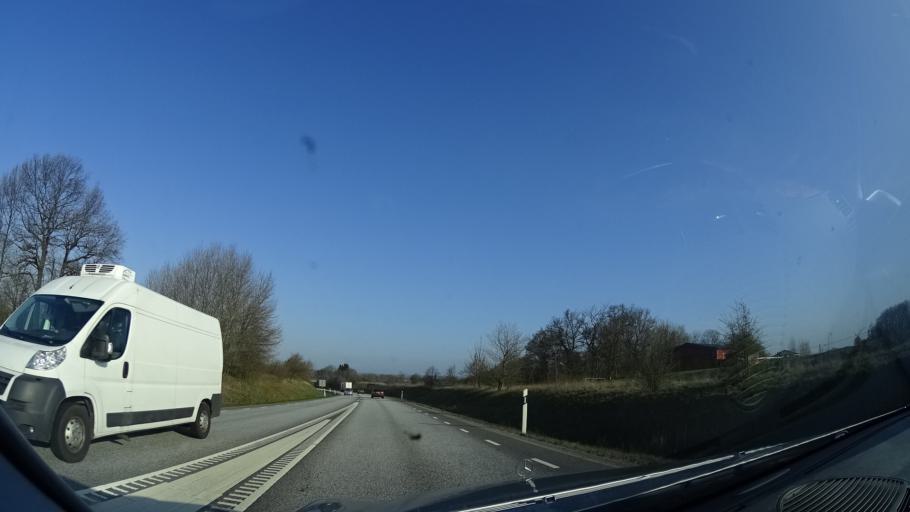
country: SE
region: Skane
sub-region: Eslovs Kommun
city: Eslov
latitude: 55.8512
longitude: 13.3183
